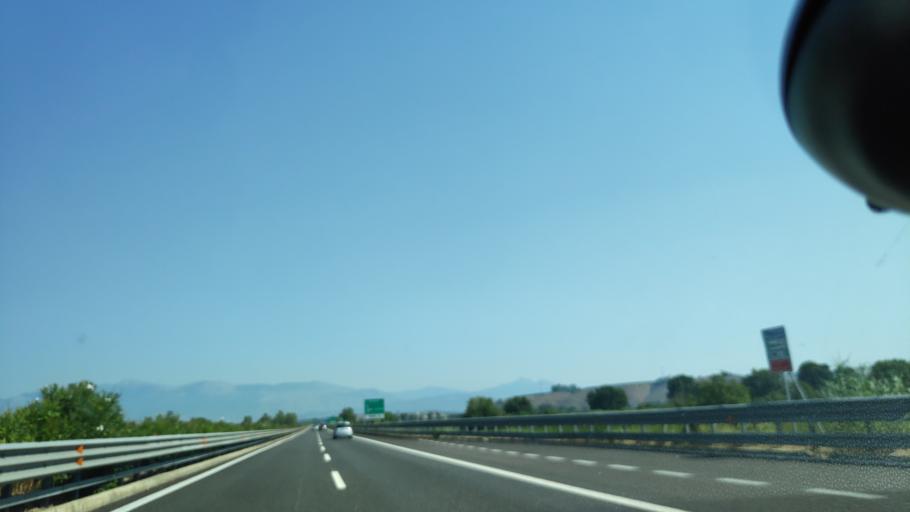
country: IT
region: Calabria
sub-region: Provincia di Cosenza
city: Roggiano Gravina
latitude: 39.6664
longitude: 16.2142
